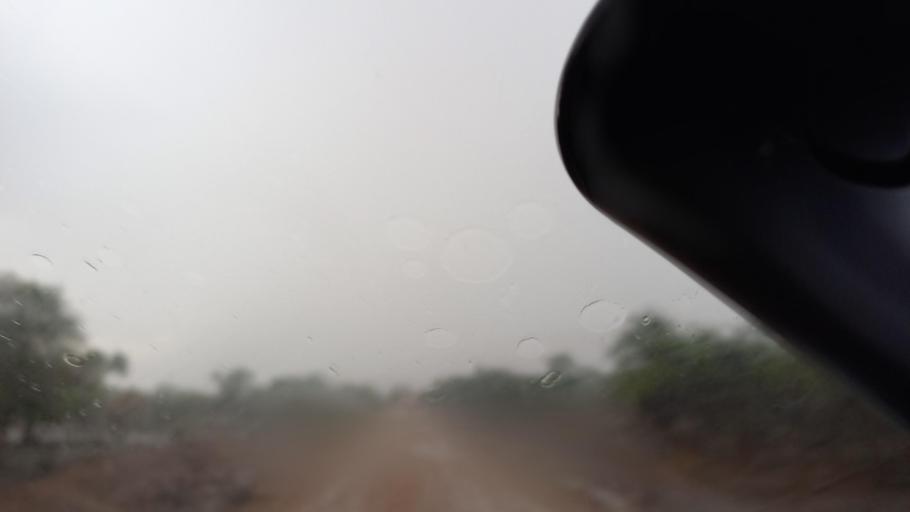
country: ZM
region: Lusaka
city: Kafue
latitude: -15.9374
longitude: 28.2117
